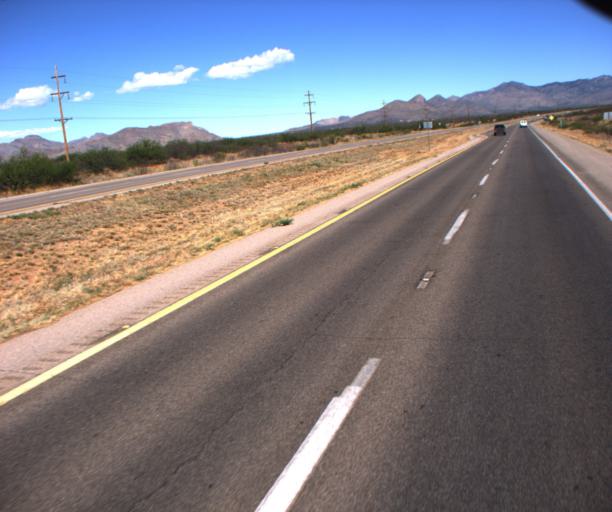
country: US
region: Arizona
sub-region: Cochise County
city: Huachuca City
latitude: 31.6547
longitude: -110.3458
